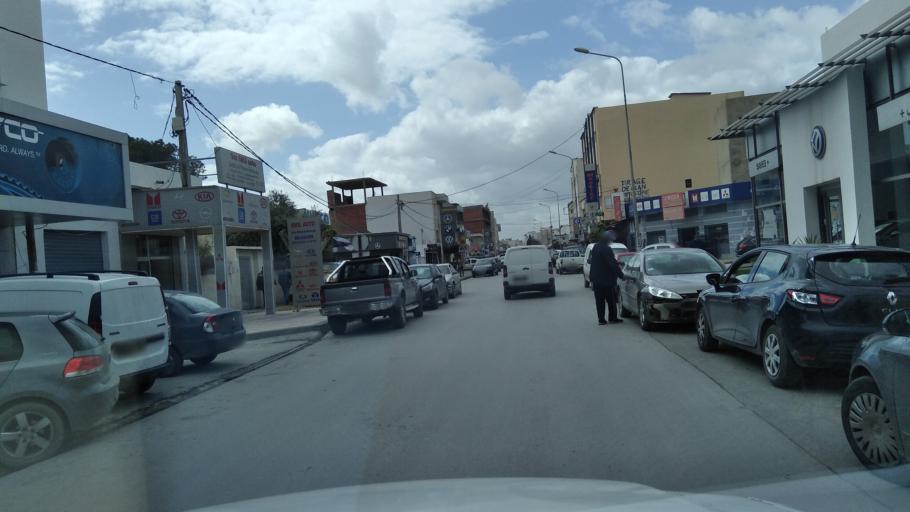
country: TN
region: Bin 'Arus
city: Ben Arous
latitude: 36.7622
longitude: 10.2253
